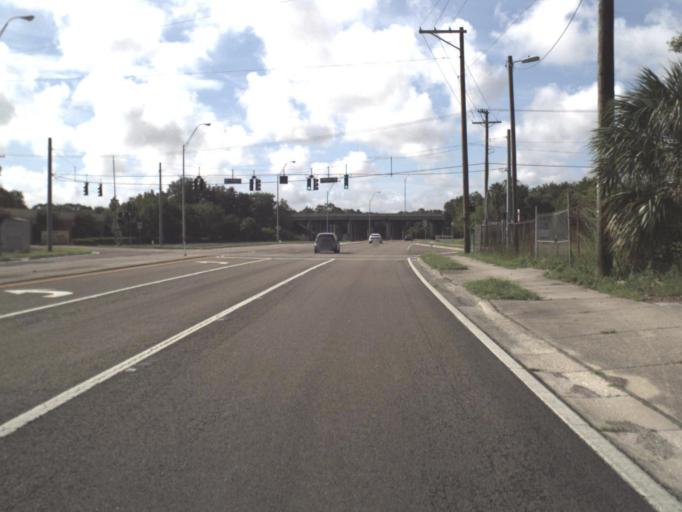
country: US
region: Florida
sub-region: Hillsborough County
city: Lake Magdalene
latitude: 28.0995
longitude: -82.4536
